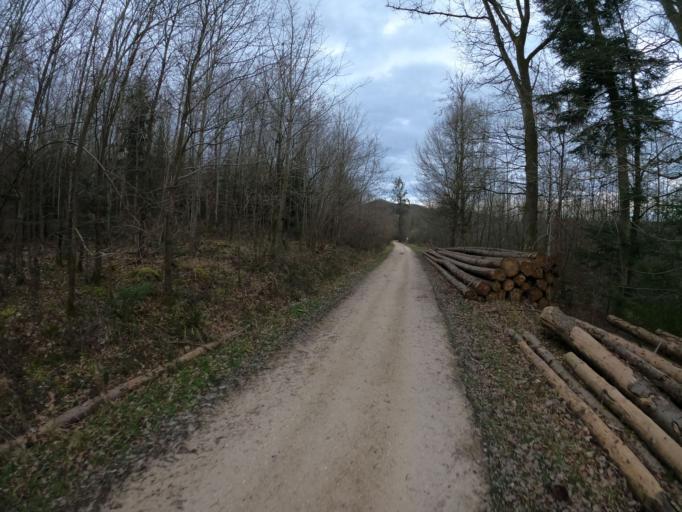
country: DE
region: Baden-Wuerttemberg
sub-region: Regierungsbezirk Stuttgart
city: Ottenbach
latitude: 48.7277
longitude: 9.7300
